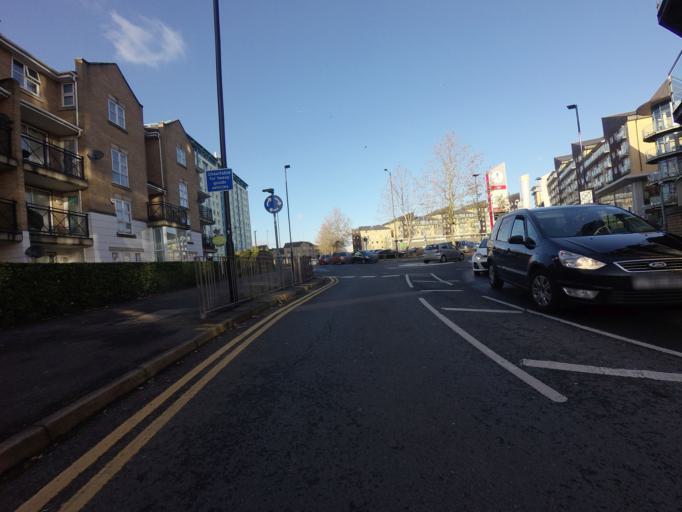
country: GB
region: England
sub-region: Greater London
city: Feltham
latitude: 51.4449
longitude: -0.4127
